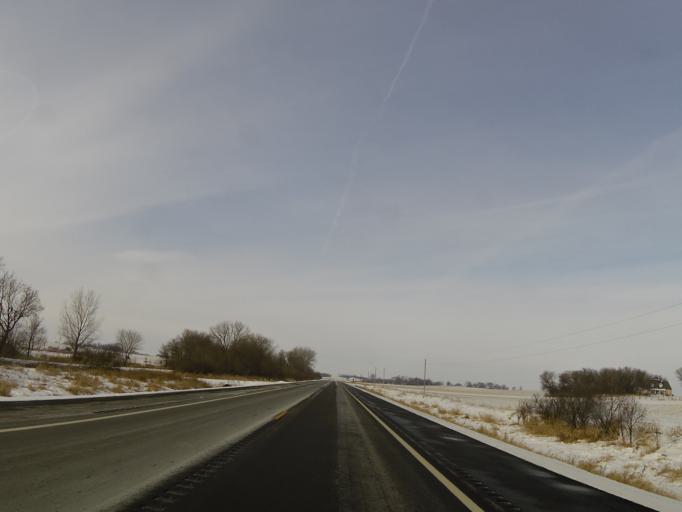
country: US
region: Minnesota
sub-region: McLeod County
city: Hutchinson
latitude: 44.9016
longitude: -94.4361
